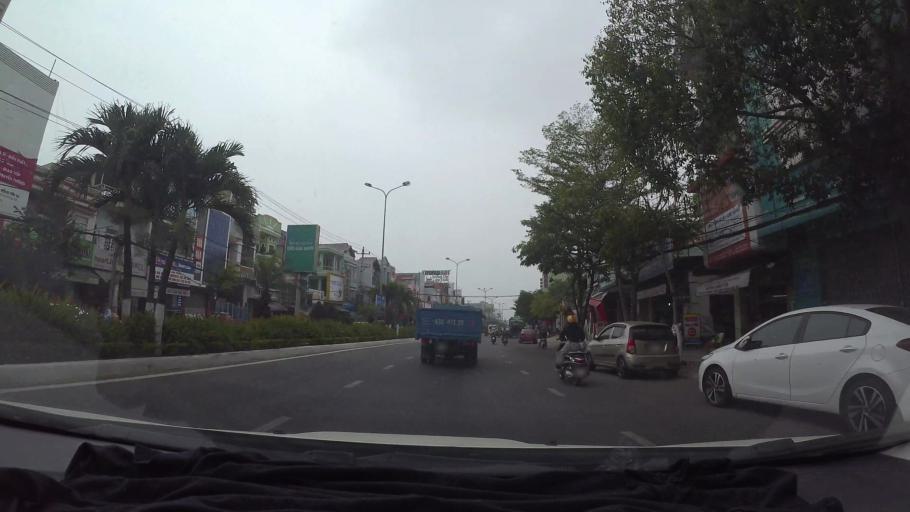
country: VN
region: Da Nang
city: Da Nang
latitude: 16.0571
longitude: 108.2069
